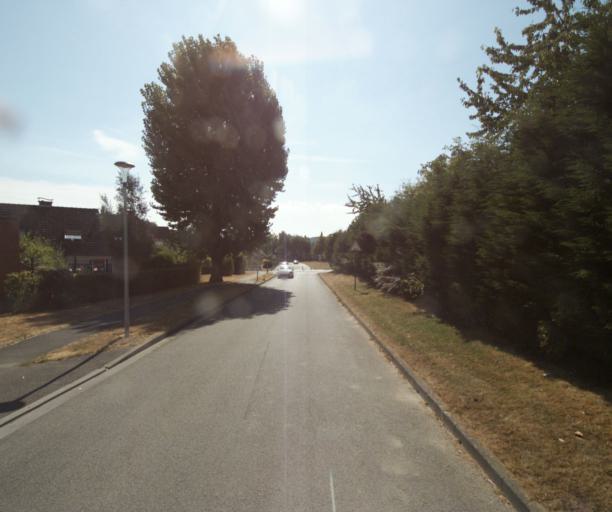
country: FR
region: Nord-Pas-de-Calais
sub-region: Departement du Nord
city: Halluin
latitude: 50.7716
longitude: 3.1183
